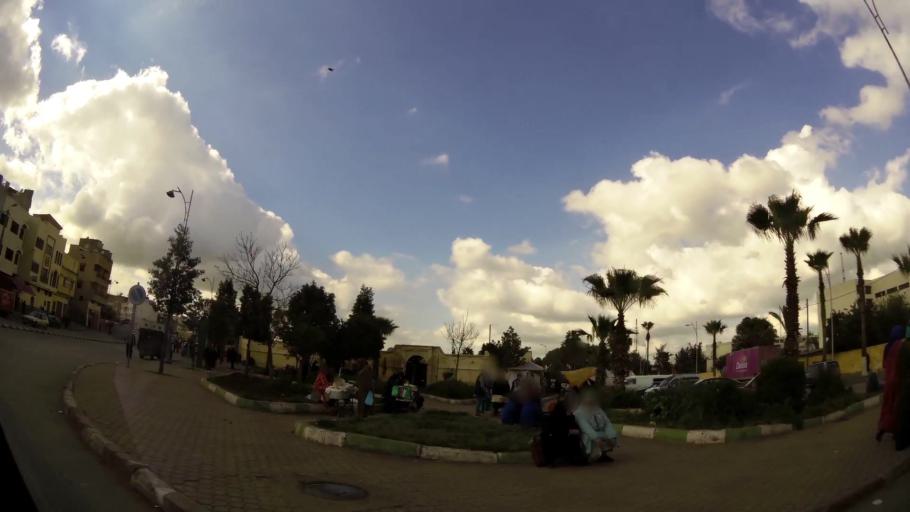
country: MA
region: Chaouia-Ouardigha
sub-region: Settat Province
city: Settat
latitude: 33.0059
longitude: -7.6209
